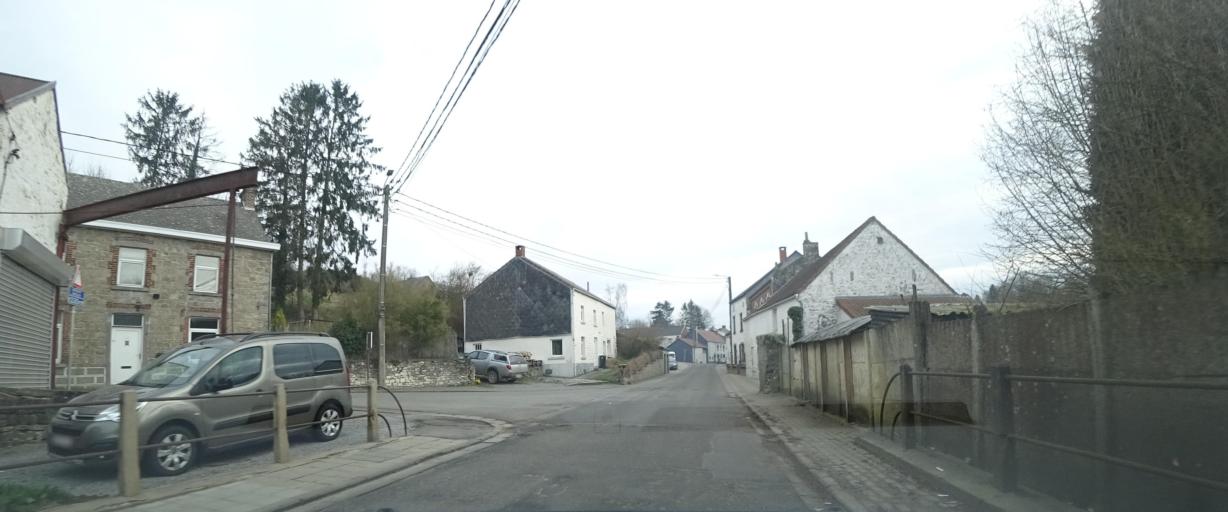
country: BE
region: Wallonia
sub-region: Province de Namur
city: Sombreffe
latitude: 50.5022
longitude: 4.6449
